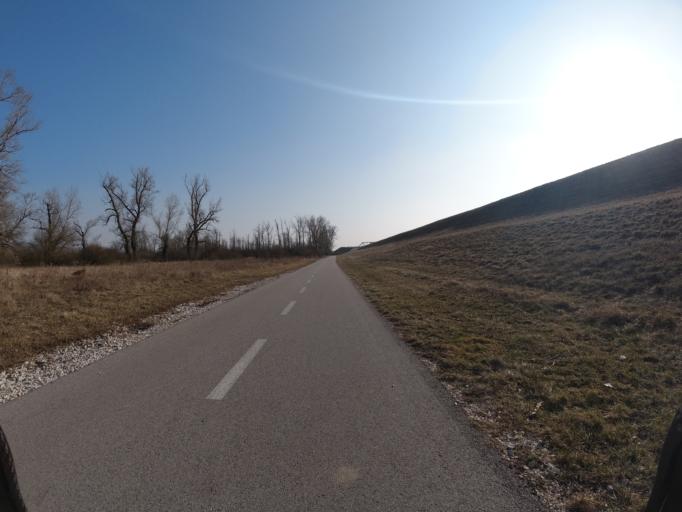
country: SK
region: Nitriansky
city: Cachtice
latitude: 48.6726
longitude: 17.8611
